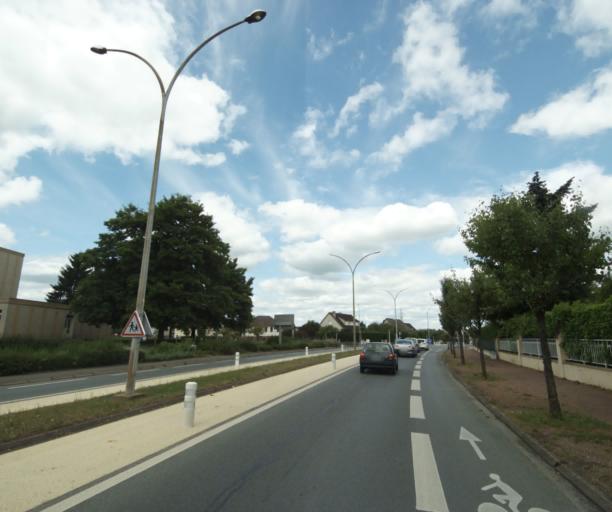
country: FR
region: Centre
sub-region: Departement d'Eure-et-Loir
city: Mainvilliers
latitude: 48.4390
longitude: 1.4505
